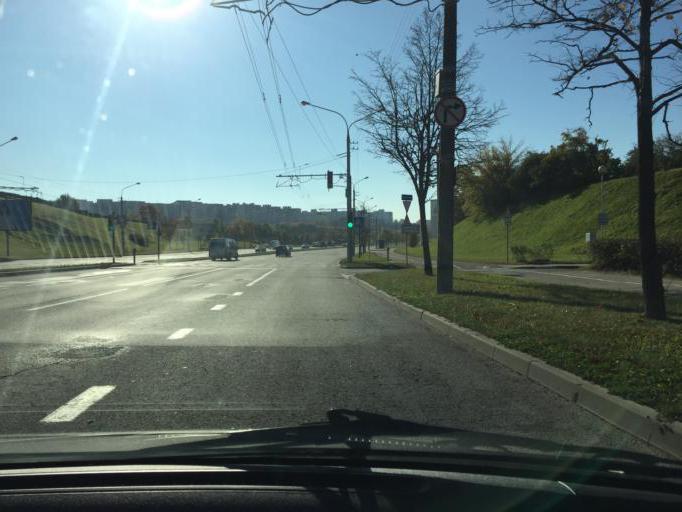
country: BY
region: Minsk
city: Syenitsa
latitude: 53.8589
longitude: 27.5381
